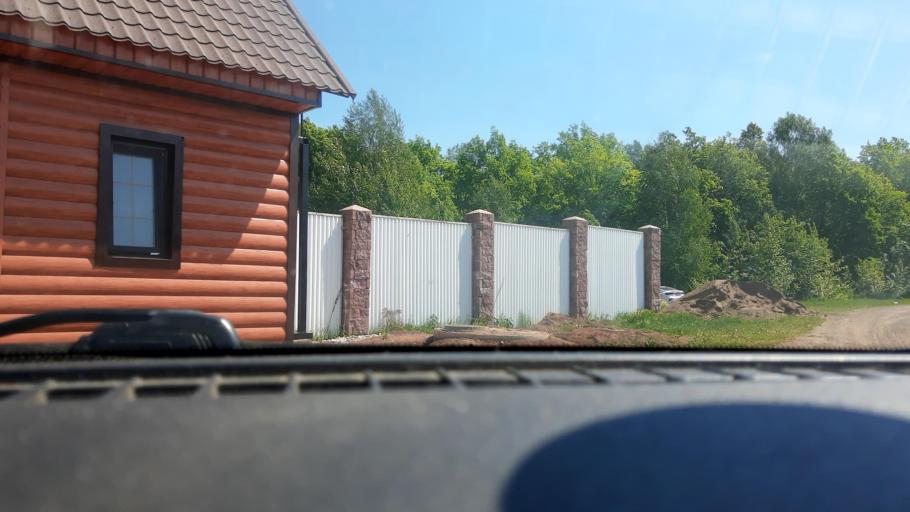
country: RU
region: Bashkortostan
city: Avdon
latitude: 54.4253
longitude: 55.8455
